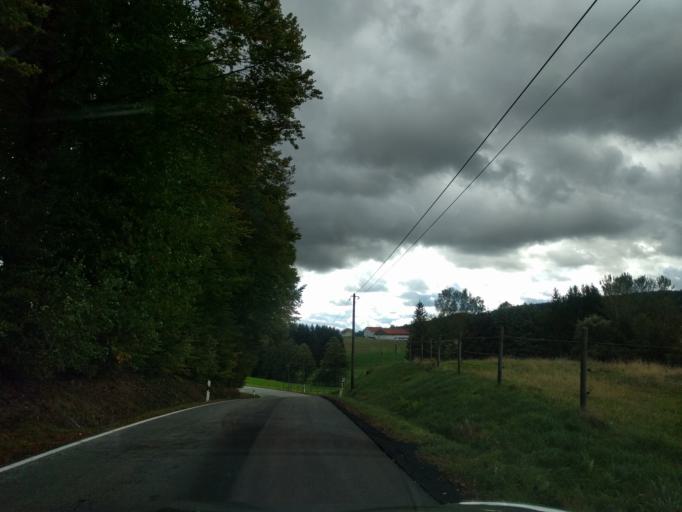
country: DE
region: Bavaria
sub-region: Lower Bavaria
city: Schaufling
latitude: 48.8401
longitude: 13.0903
